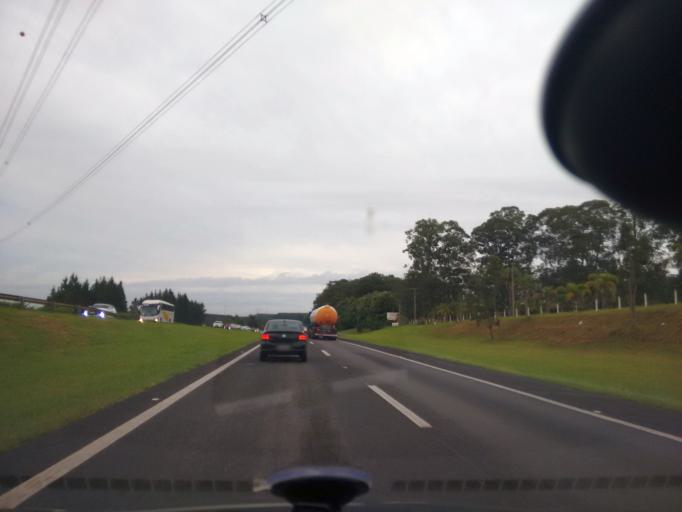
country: BR
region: Sao Paulo
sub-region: Itirapina
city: Itirapina
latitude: -22.1558
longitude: -47.7931
